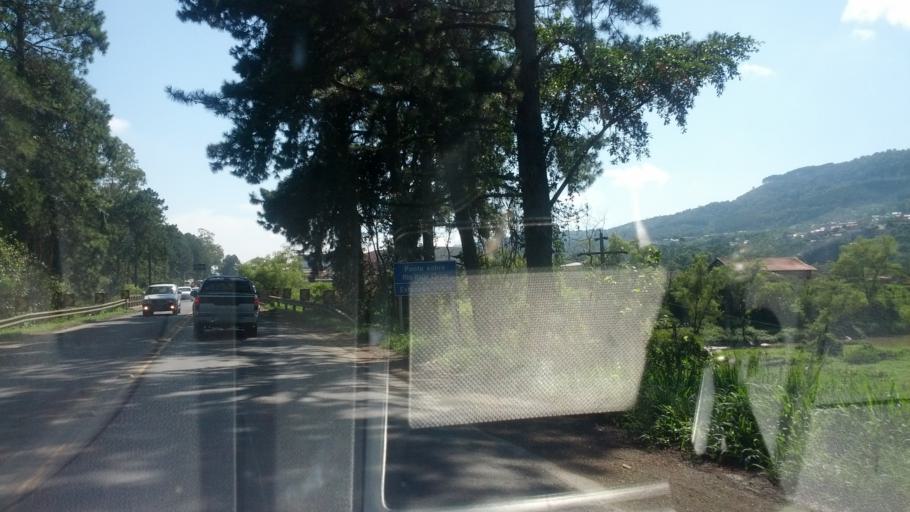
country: BR
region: Santa Catarina
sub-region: Rio Do Sul
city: Rio do Sul
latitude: -27.2450
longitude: -49.6924
